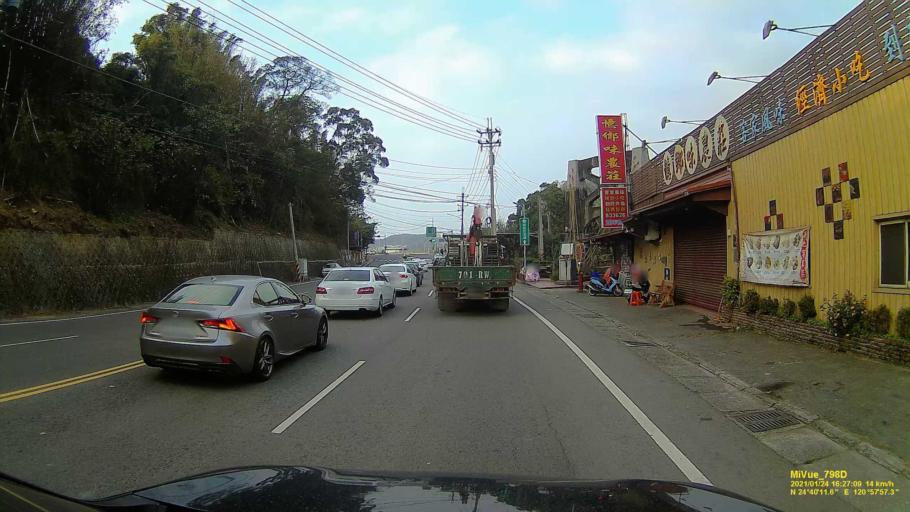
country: TW
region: Taiwan
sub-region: Hsinchu
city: Hsinchu
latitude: 24.6701
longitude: 120.9659
